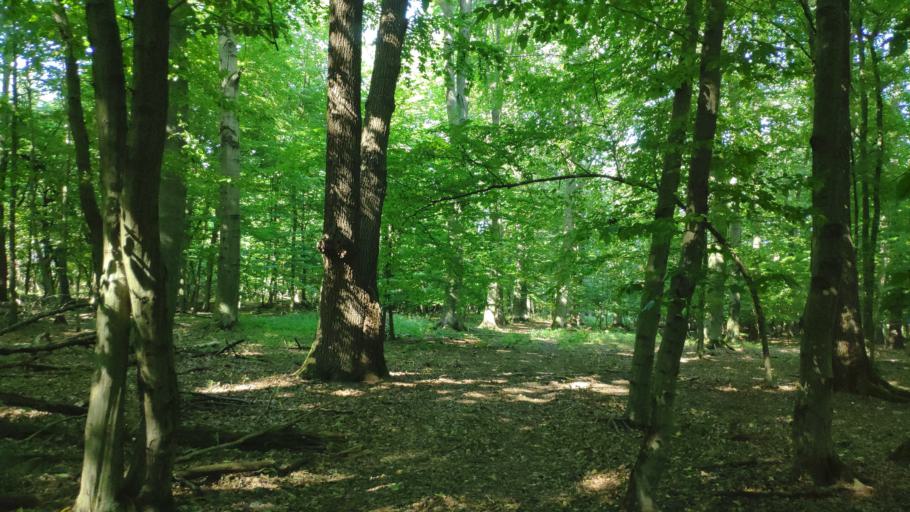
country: SK
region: Presovsky
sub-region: Okres Presov
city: Presov
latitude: 48.9044
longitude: 21.2957
